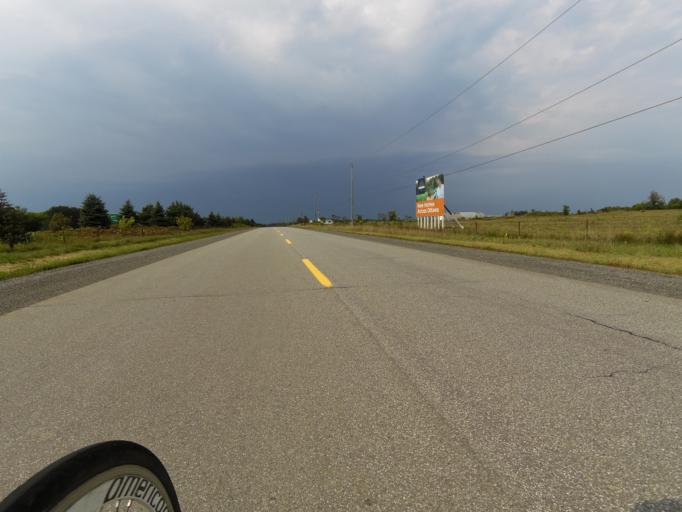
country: CA
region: Ontario
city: Bells Corners
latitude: 45.2323
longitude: -75.7515
